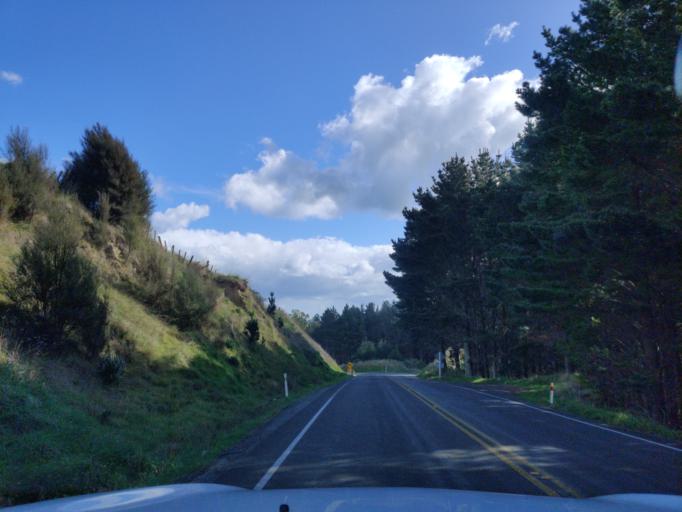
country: NZ
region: Manawatu-Wanganui
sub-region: Palmerston North City
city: Palmerston North
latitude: -40.2861
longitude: 175.7915
